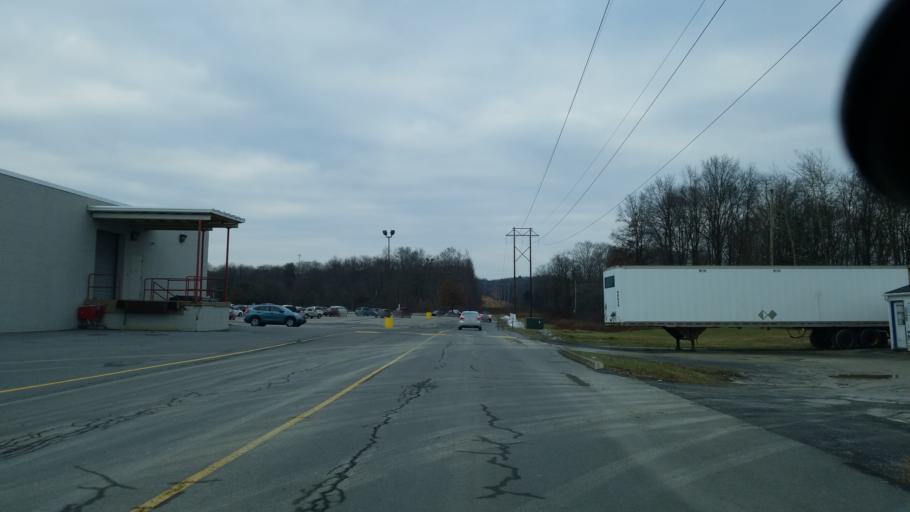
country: US
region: Pennsylvania
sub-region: Clearfield County
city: DuBois
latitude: 41.1193
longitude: -78.7281
